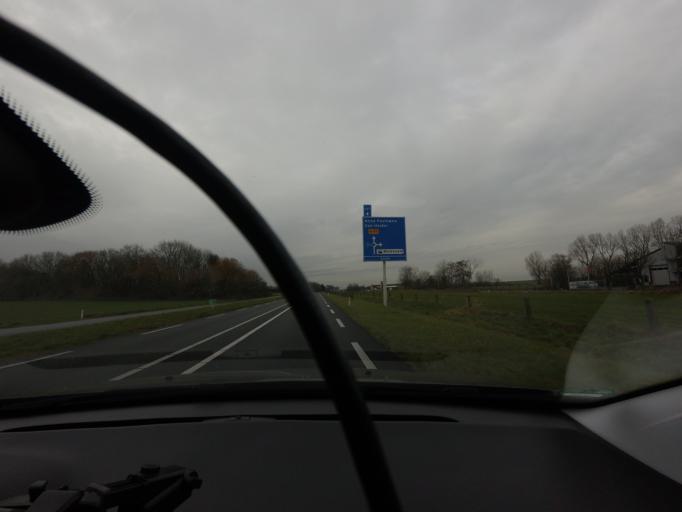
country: NL
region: North Holland
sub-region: Gemeente Hollands Kroon
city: Den Oever
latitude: 52.8995
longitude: 4.9475
